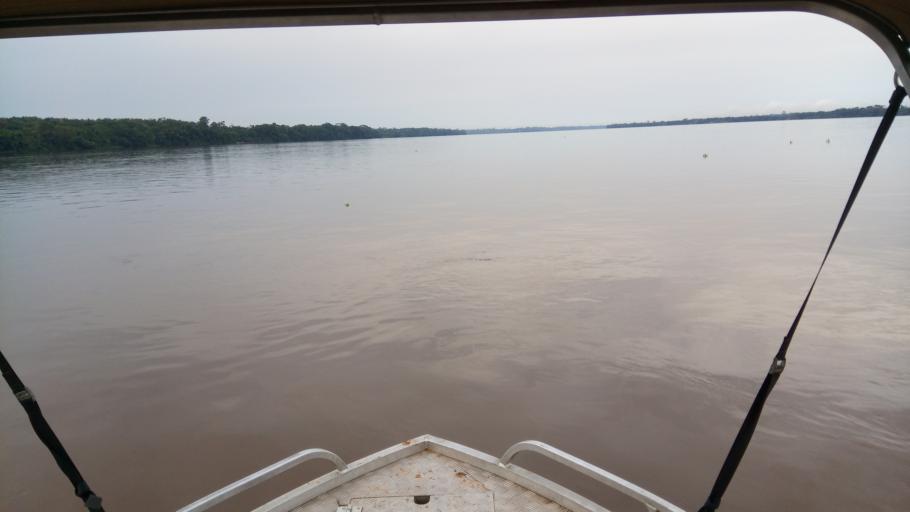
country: CD
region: Eastern Province
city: Kisangani
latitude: 0.5745
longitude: 24.8273
